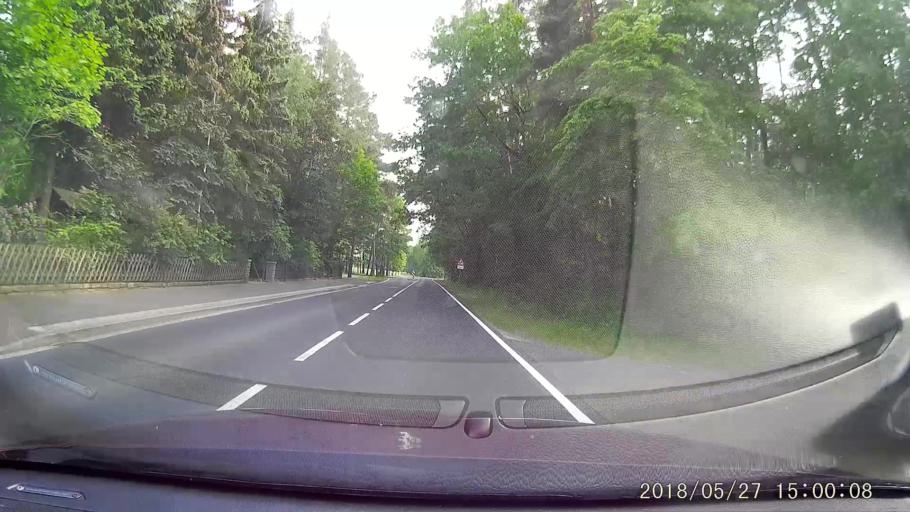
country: DE
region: Saxony
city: Mucka
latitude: 51.3426
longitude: 14.6859
